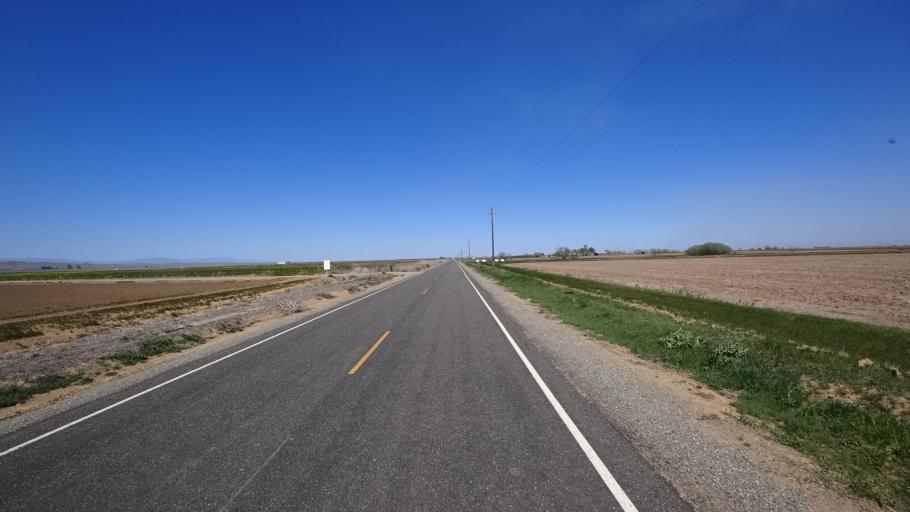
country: US
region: California
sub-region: Glenn County
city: Willows
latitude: 39.4210
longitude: -122.2485
